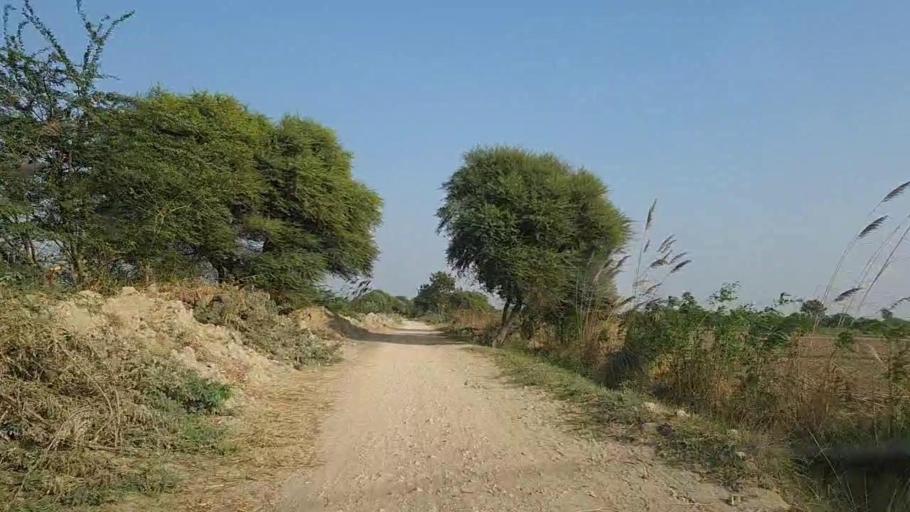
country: PK
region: Sindh
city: Mirpur Sakro
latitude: 24.5999
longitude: 67.6514
